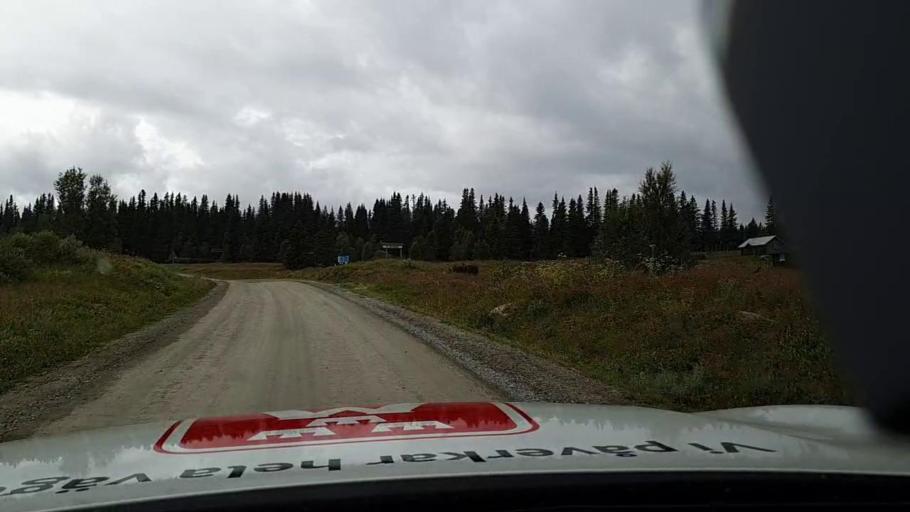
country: SE
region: Jaemtland
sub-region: Are Kommun
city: Jarpen
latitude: 62.8389
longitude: 13.8205
